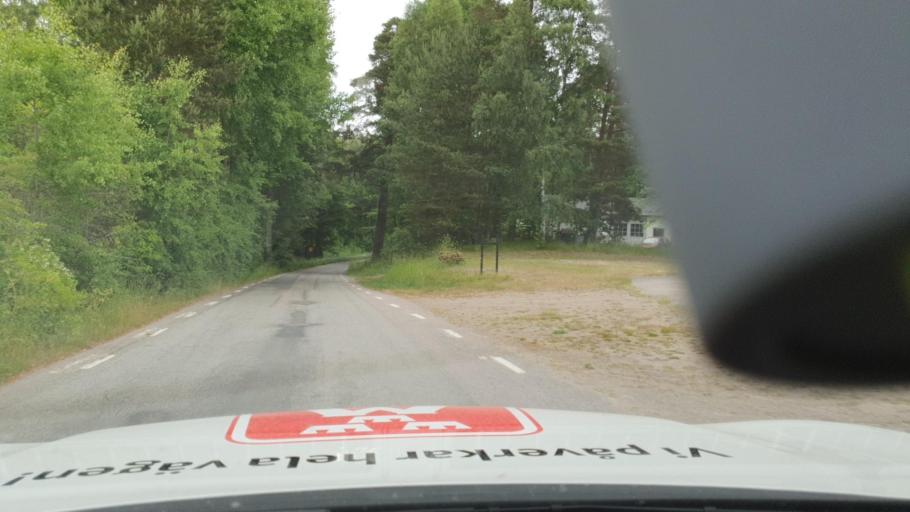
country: SE
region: Vaestra Goetaland
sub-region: Hjo Kommun
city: Hjo
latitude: 58.1799
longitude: 14.1985
